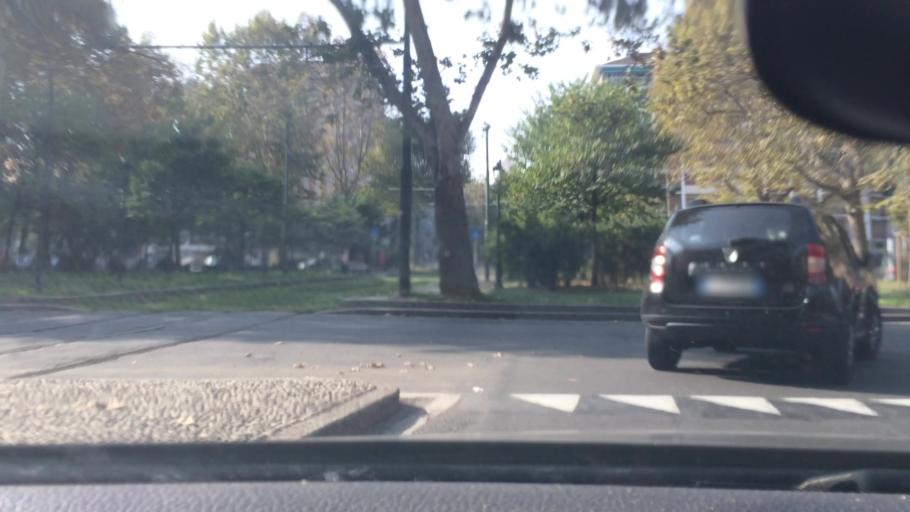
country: IT
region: Lombardy
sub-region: Citta metropolitana di Milano
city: Milano
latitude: 45.4878
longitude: 9.1622
